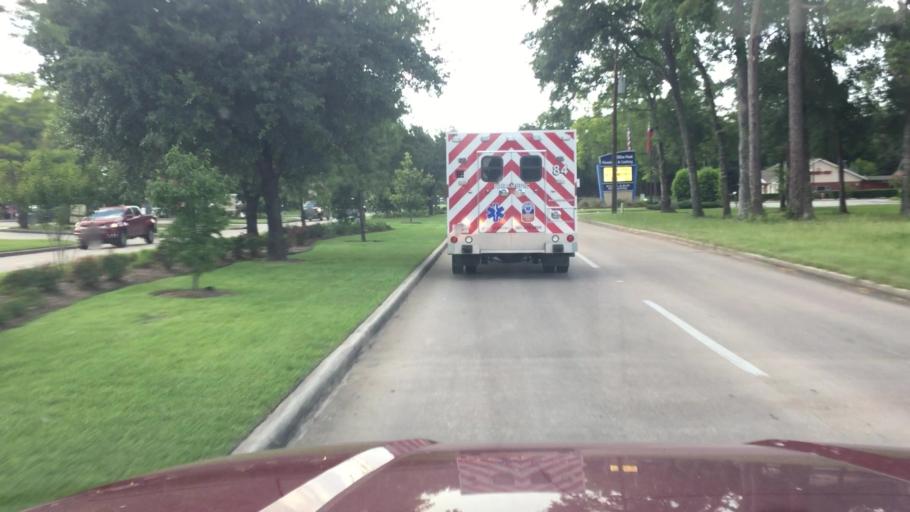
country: US
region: Texas
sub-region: Harris County
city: Tomball
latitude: 30.0254
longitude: -95.5288
